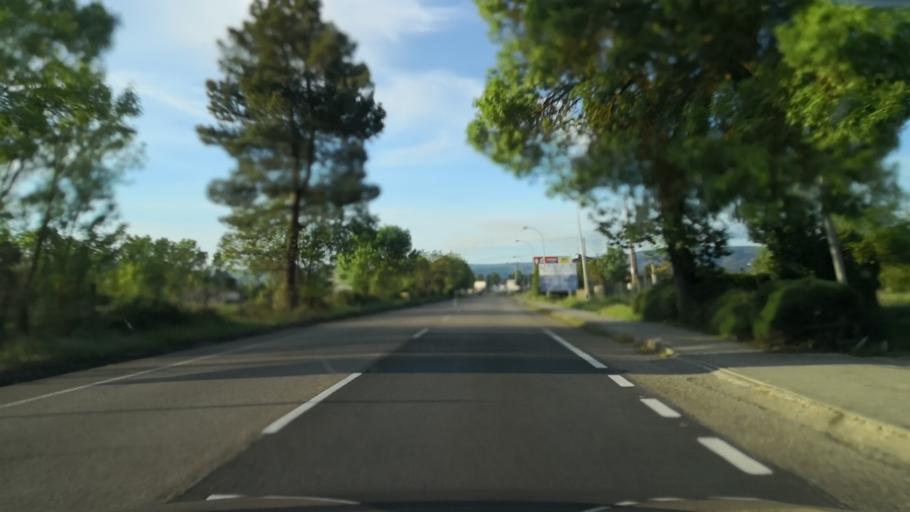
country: ES
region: Galicia
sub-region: Provincia de Ourense
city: Verin
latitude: 41.9239
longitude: -7.4429
